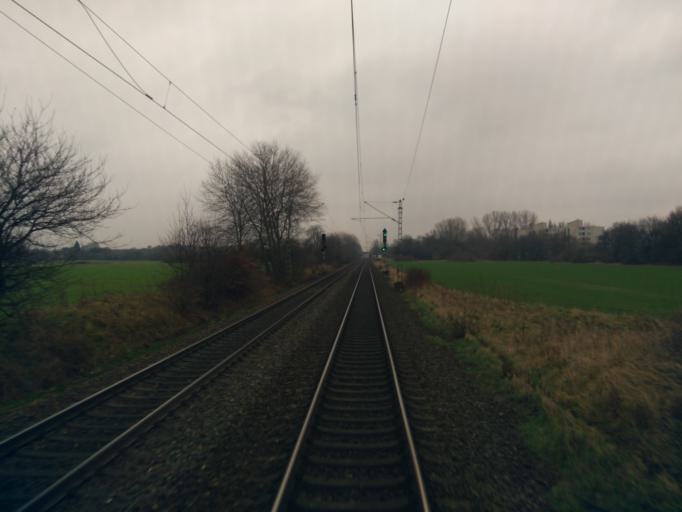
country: DE
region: Lower Saxony
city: Riede
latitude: 53.0431
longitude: 8.9335
